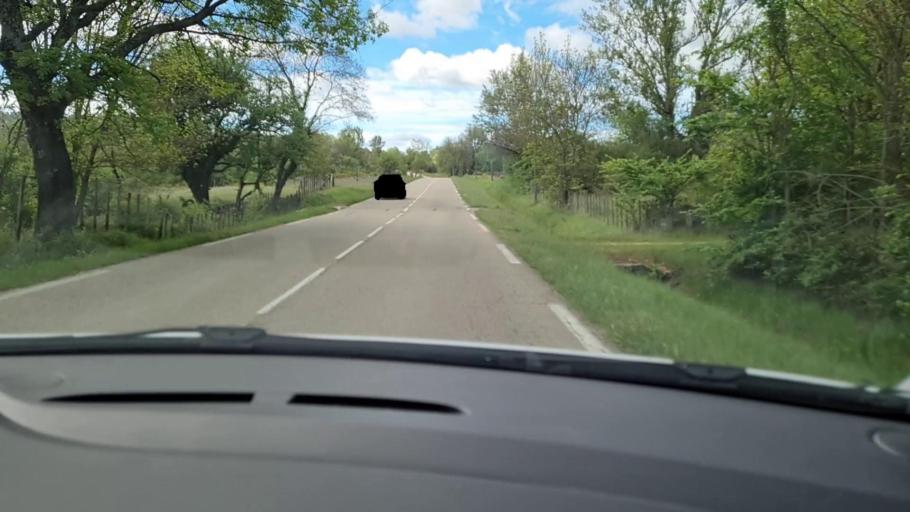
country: FR
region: Languedoc-Roussillon
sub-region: Departement du Gard
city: Quissac
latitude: 43.8669
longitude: 4.0157
